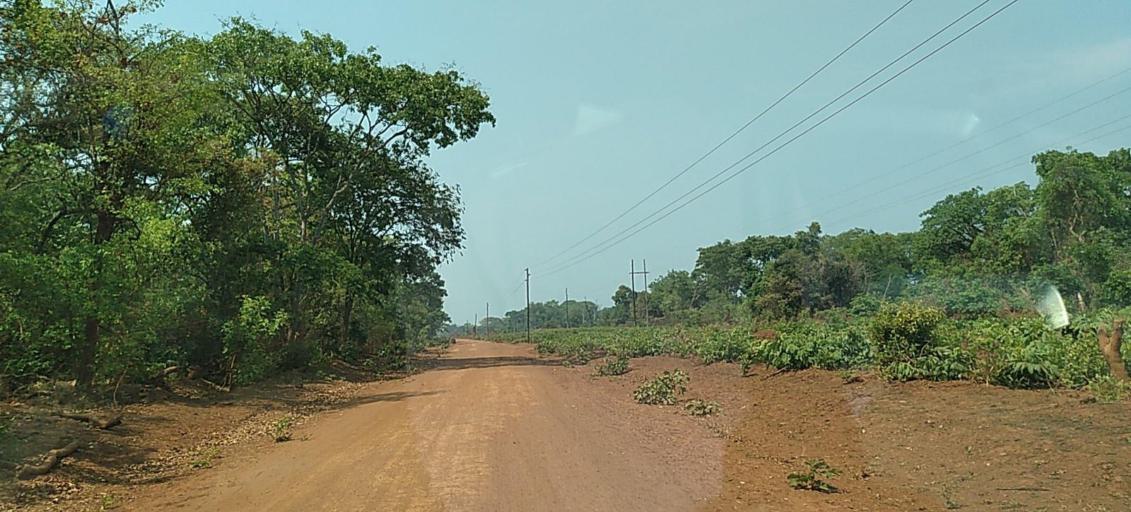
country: ZM
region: Copperbelt
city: Chingola
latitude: -13.0724
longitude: 27.4143
